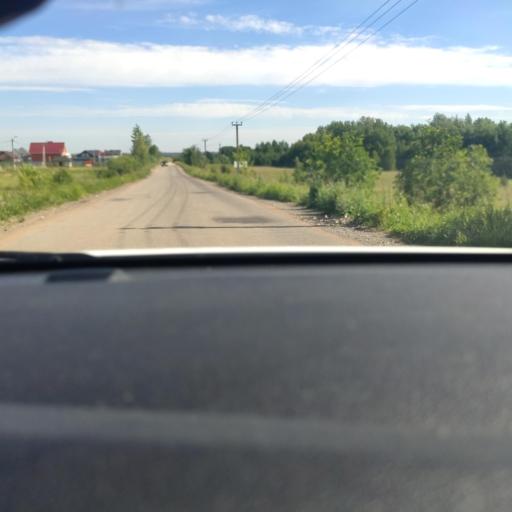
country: RU
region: Tatarstan
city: Vysokaya Gora
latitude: 55.8193
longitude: 49.3121
